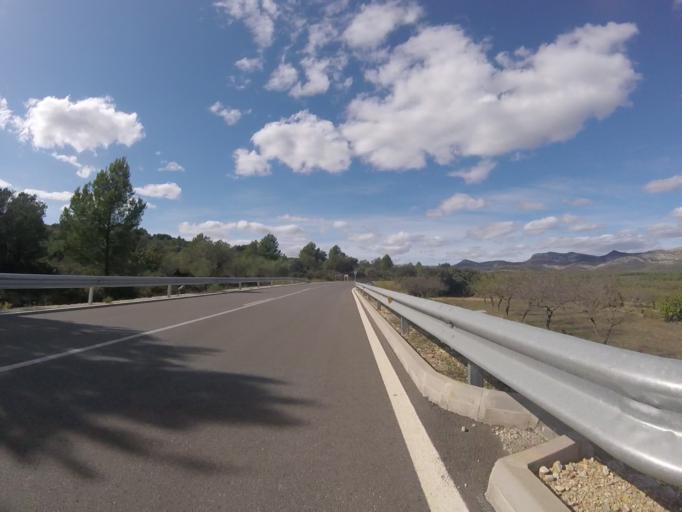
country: ES
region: Valencia
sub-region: Provincia de Castello
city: Chert/Xert
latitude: 40.4384
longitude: 0.1141
